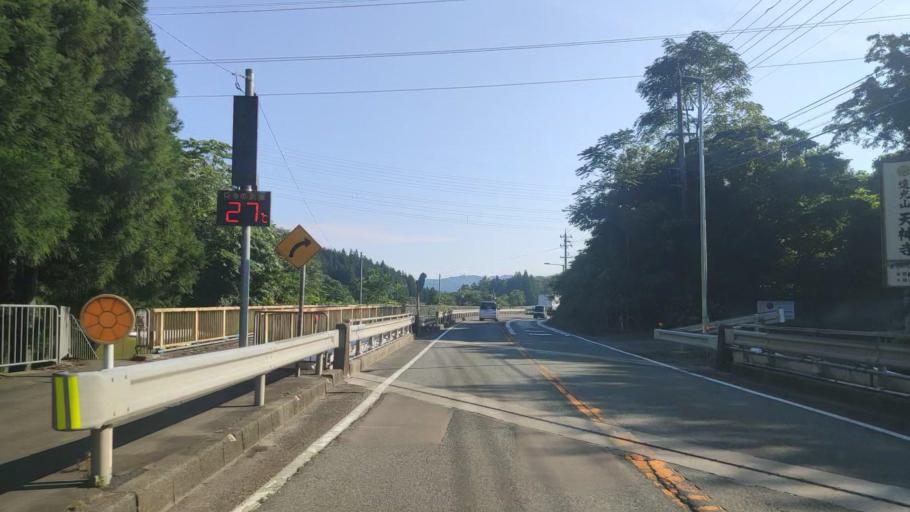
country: JP
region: Fukui
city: Maruoka
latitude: 36.2236
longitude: 136.2784
